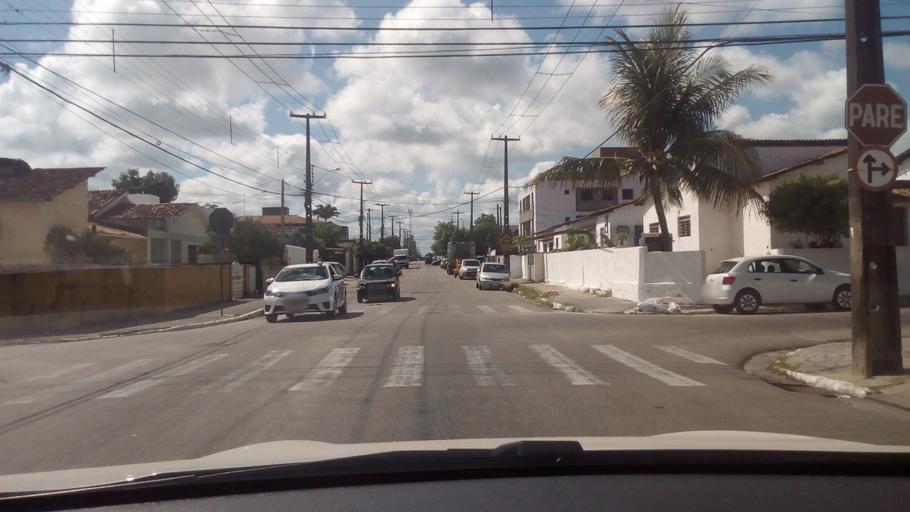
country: BR
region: Paraiba
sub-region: Joao Pessoa
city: Joao Pessoa
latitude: -7.1296
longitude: -34.8644
